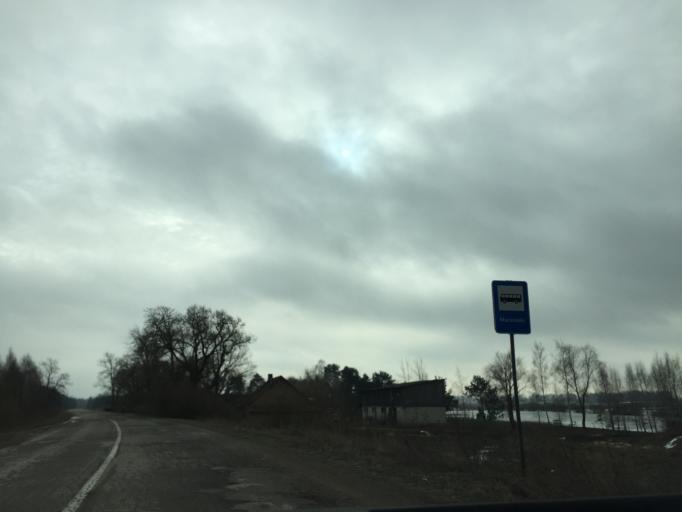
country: LV
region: Rundales
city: Pilsrundale
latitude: 56.5483
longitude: 23.9875
